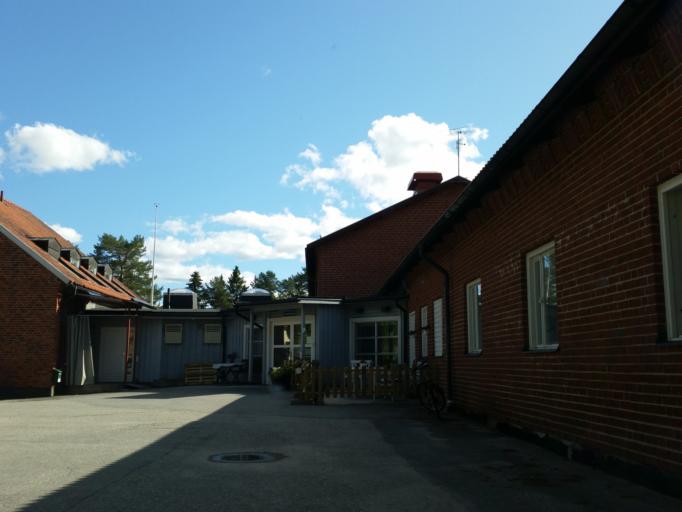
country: SE
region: Vaesterbotten
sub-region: Robertsfors Kommun
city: Robertsfors
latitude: 64.1962
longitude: 20.8496
